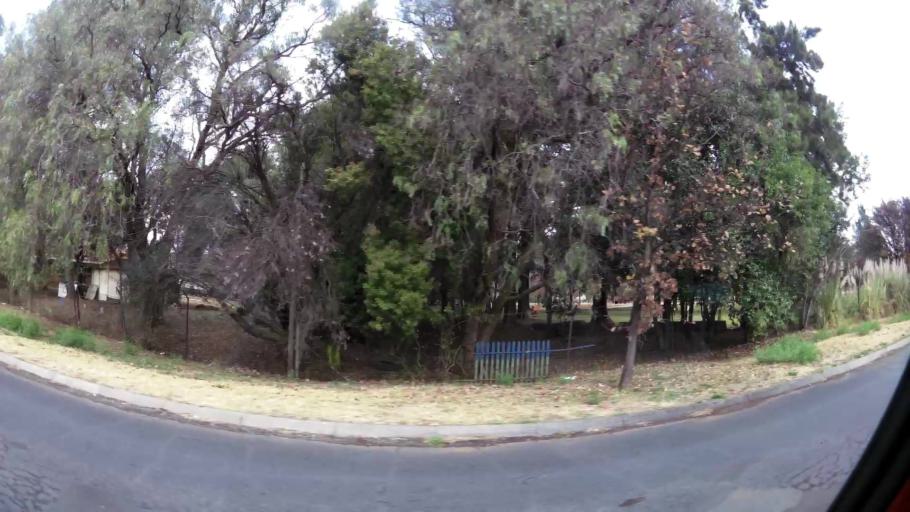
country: ZA
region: Gauteng
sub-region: Sedibeng District Municipality
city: Vanderbijlpark
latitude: -26.7424
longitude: 27.8505
